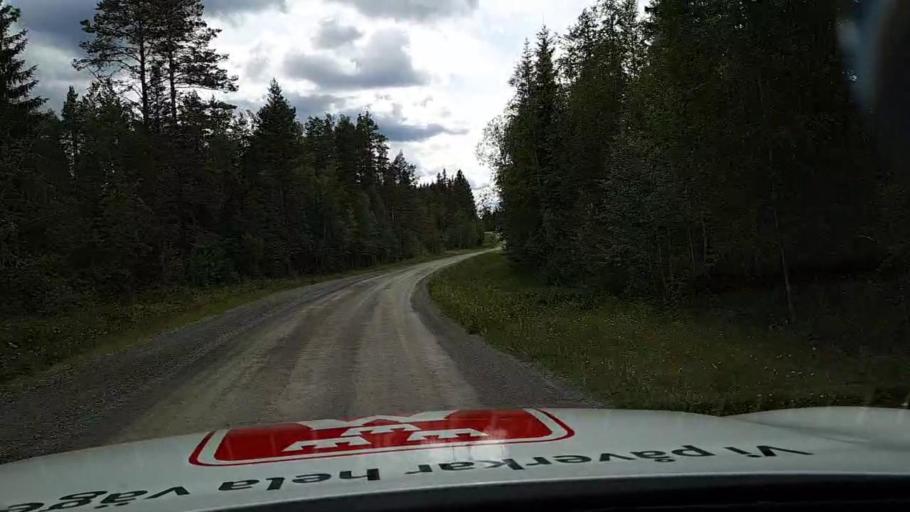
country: SE
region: Jaemtland
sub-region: Braecke Kommun
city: Braecke
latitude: 63.2637
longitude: 15.3776
